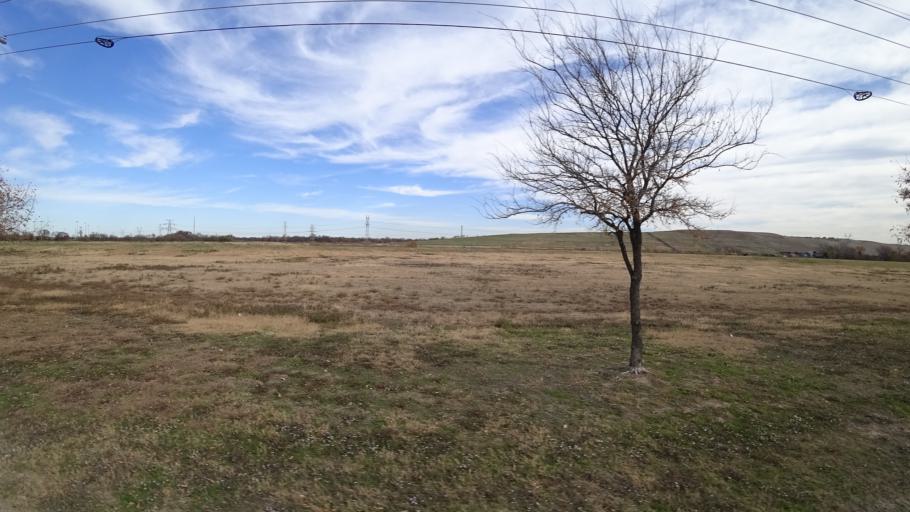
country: US
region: Texas
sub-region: Denton County
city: Lewisville
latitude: 33.0234
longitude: -96.9686
